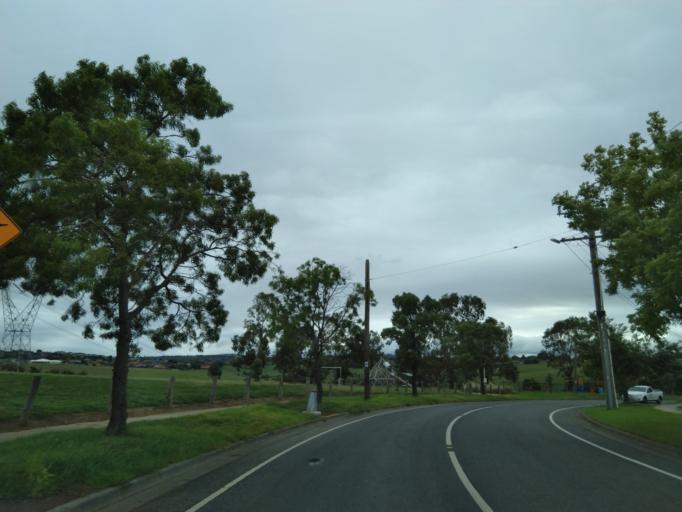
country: AU
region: Victoria
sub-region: Hume
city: Broadmeadows
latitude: -37.6692
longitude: 144.9062
